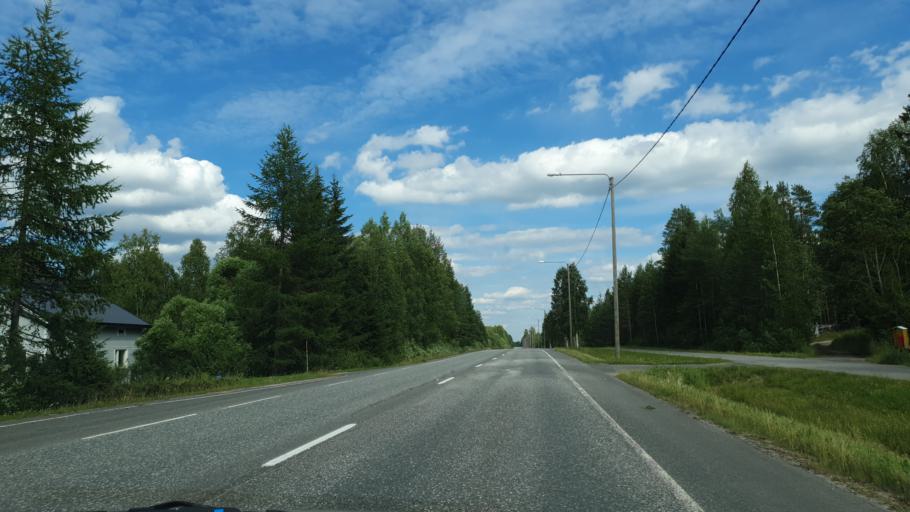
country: FI
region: Kainuu
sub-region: Kajaani
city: Kajaani
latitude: 64.2514
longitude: 27.7873
